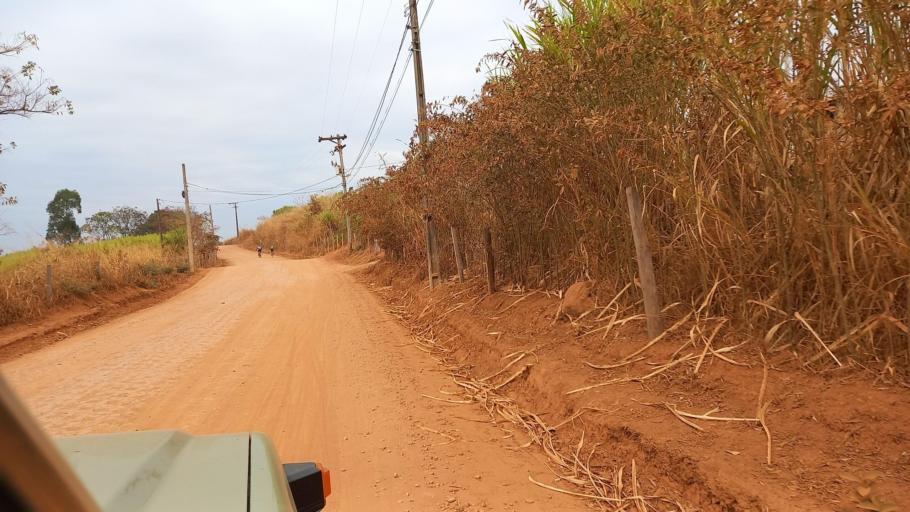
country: BR
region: Sao Paulo
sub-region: Moji-Guacu
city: Mogi-Gaucu
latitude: -22.3257
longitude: -46.8576
